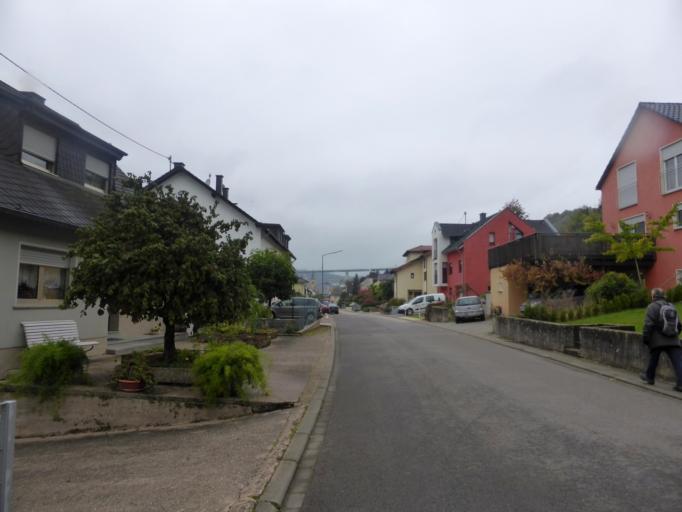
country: DE
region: Rheinland-Pfalz
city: Oberbillig
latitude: 49.7246
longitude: 6.5184
